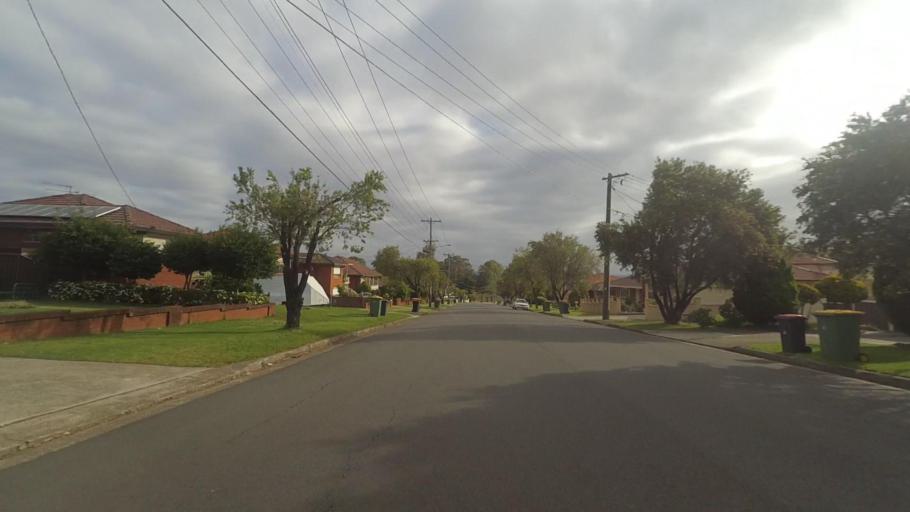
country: AU
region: New South Wales
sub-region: Bankstown
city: Milperra
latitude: -33.9129
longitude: 150.9999
